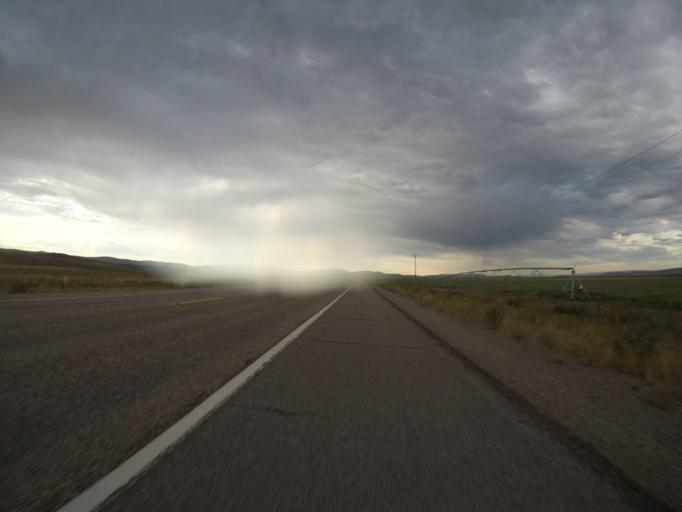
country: US
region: Utah
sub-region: Rich County
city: Randolph
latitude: 41.9282
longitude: -110.9549
